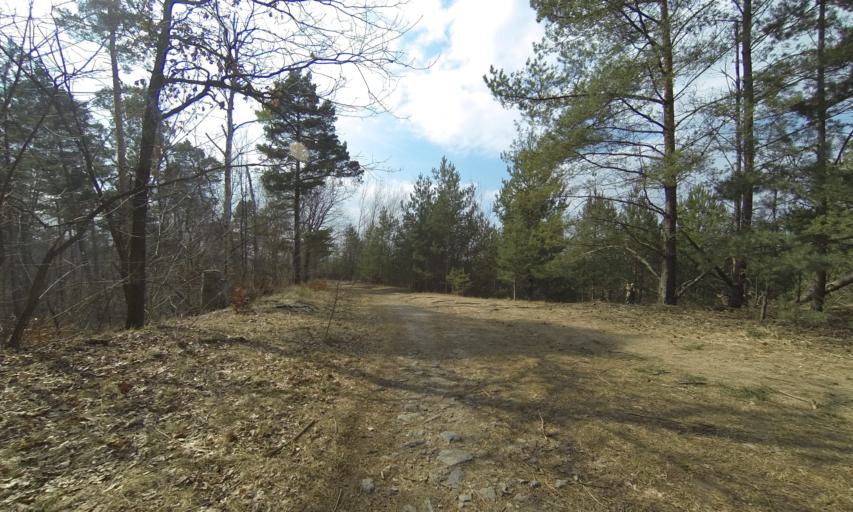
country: DE
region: Saxony
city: Albertstadt
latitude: 51.0896
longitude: 13.7817
